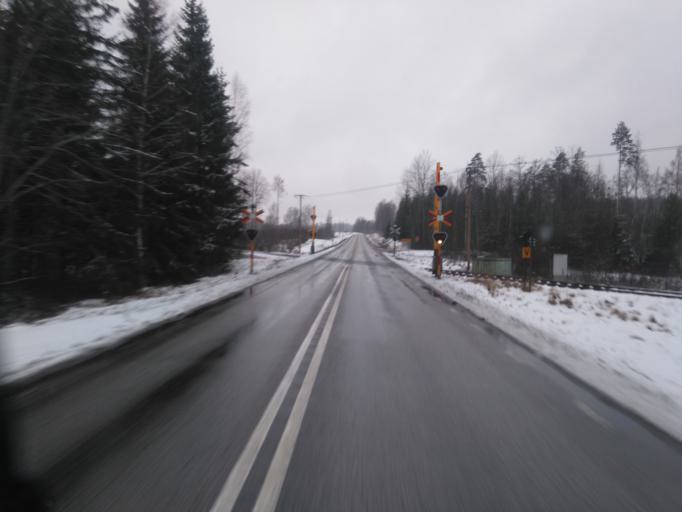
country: SE
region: Joenkoeping
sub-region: Eksjo Kommun
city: Eksjoe
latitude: 57.6506
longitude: 15.0408
